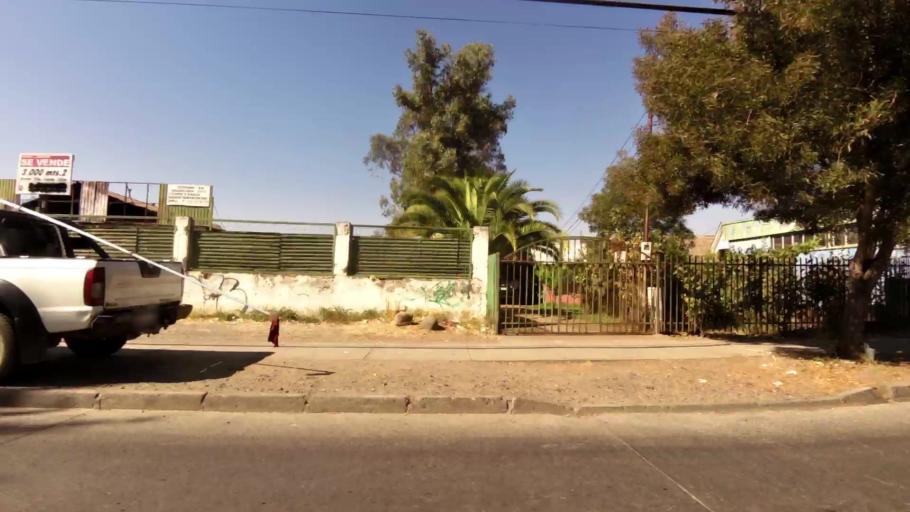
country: CL
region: Maule
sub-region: Provincia de Curico
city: Curico
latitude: -34.9811
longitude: -71.2506
